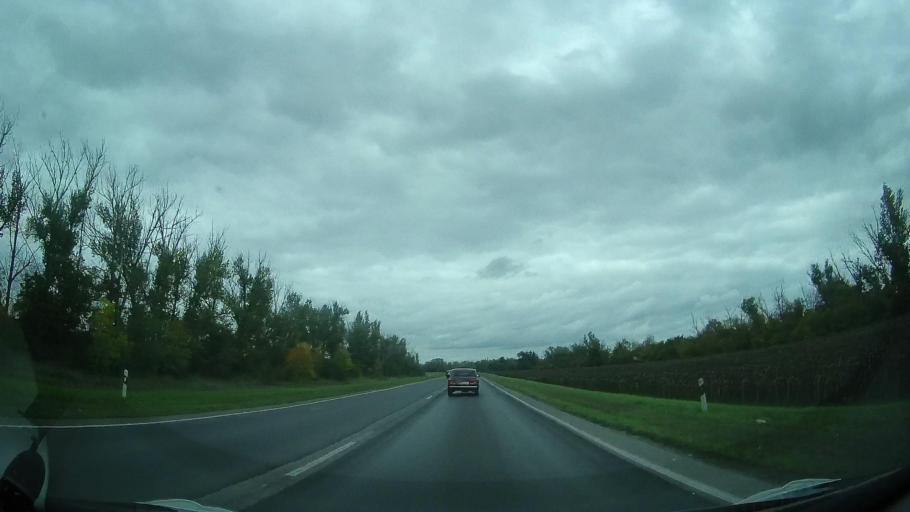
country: RU
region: Rostov
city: Yegorlykskaya
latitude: 46.5405
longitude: 40.7749
